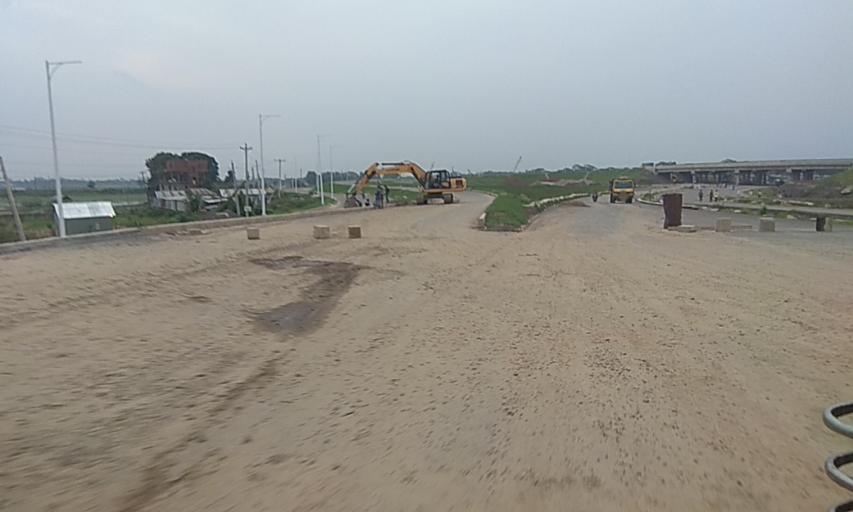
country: BD
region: Dhaka
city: Faridpur
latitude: 23.3926
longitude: 89.9826
